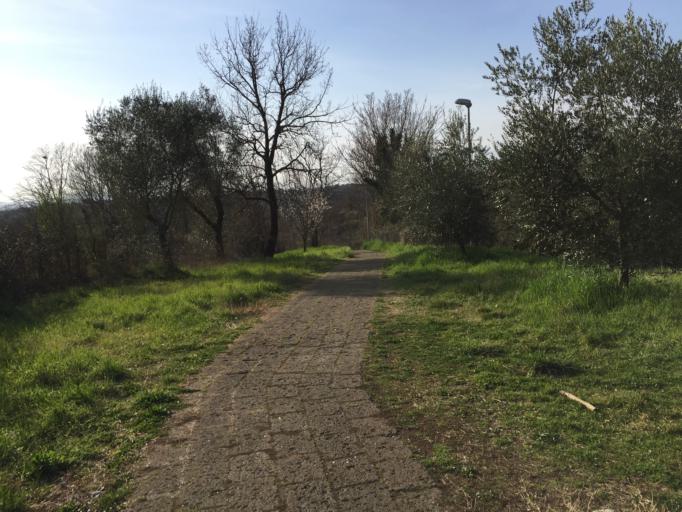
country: IT
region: Latium
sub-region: Provincia di Viterbo
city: Calcata Nuova
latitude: 42.2163
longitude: 12.4254
